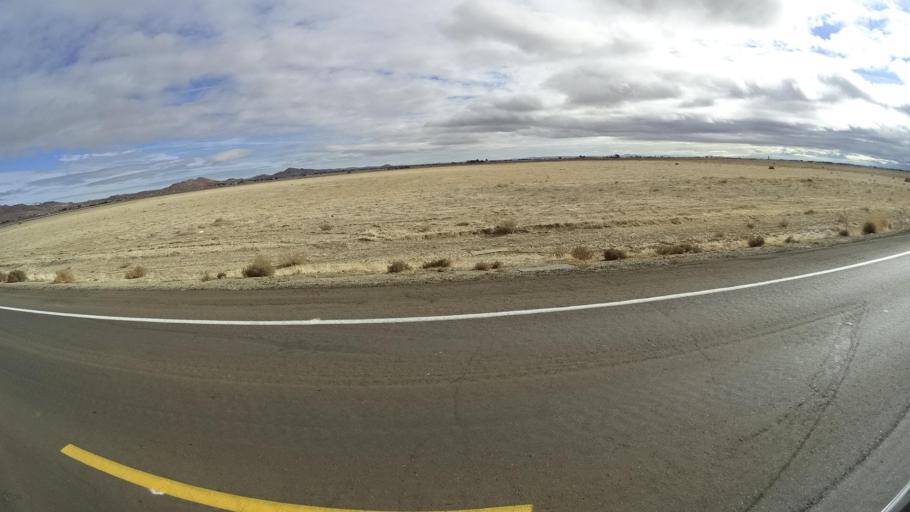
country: US
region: California
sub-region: Kern County
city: Rosamond
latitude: 34.8478
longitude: -118.2909
